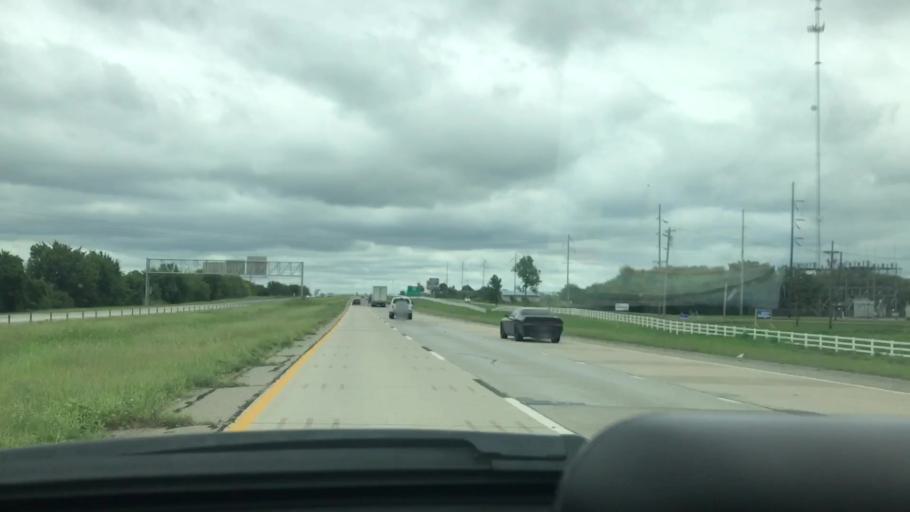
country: US
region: Oklahoma
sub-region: McIntosh County
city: Checotah
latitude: 35.4633
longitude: -95.5416
